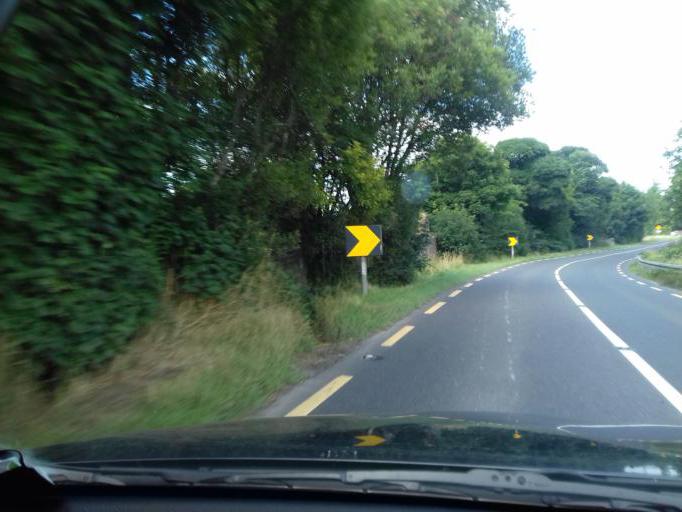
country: IE
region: Leinster
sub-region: Wicklow
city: Valleymount
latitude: 53.1360
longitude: -6.5670
